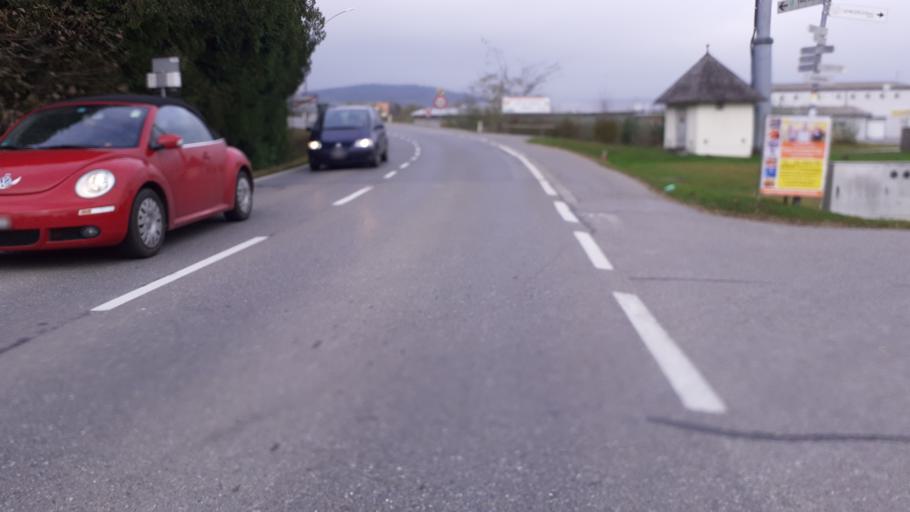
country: AT
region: Vorarlberg
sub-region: Politischer Bezirk Feldkirch
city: Meiningen
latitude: 47.3035
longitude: 9.5742
